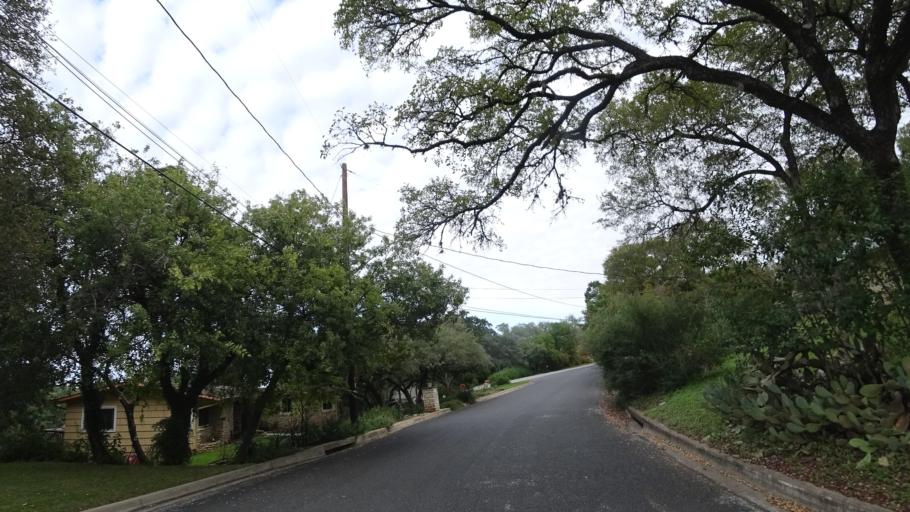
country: US
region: Texas
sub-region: Travis County
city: Rollingwood
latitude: 30.2806
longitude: -97.7900
